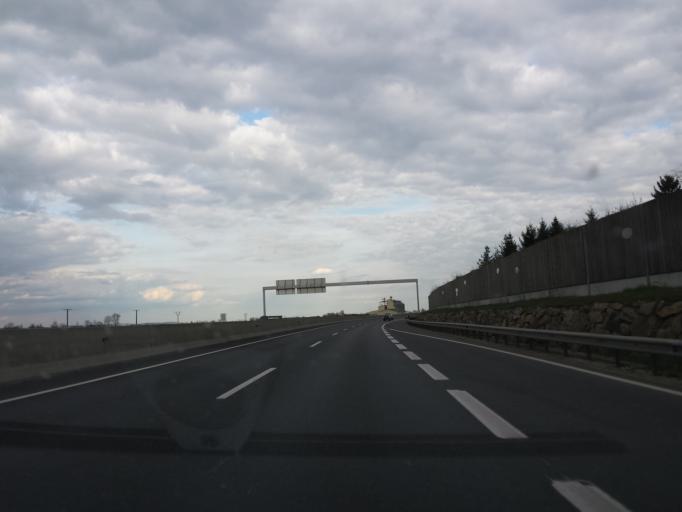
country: AT
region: Lower Austria
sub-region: Politischer Bezirk Tulln
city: Grafenworth
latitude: 48.4117
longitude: 15.7799
